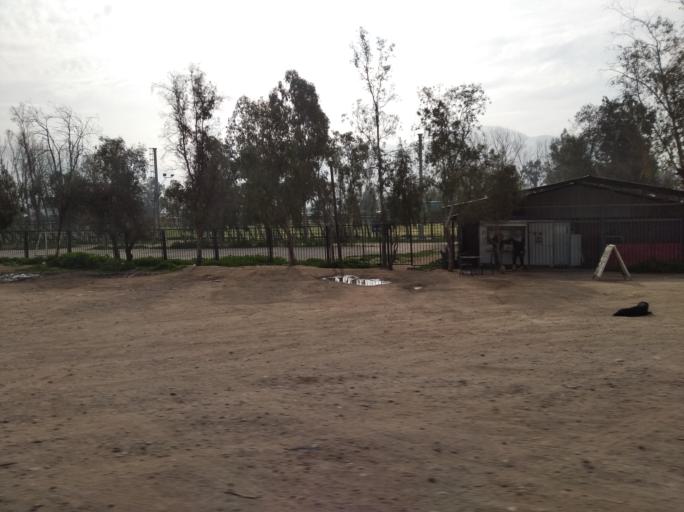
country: CL
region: Santiago Metropolitan
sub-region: Provincia de Chacabuco
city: Lampa
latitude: -33.2743
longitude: -70.8901
